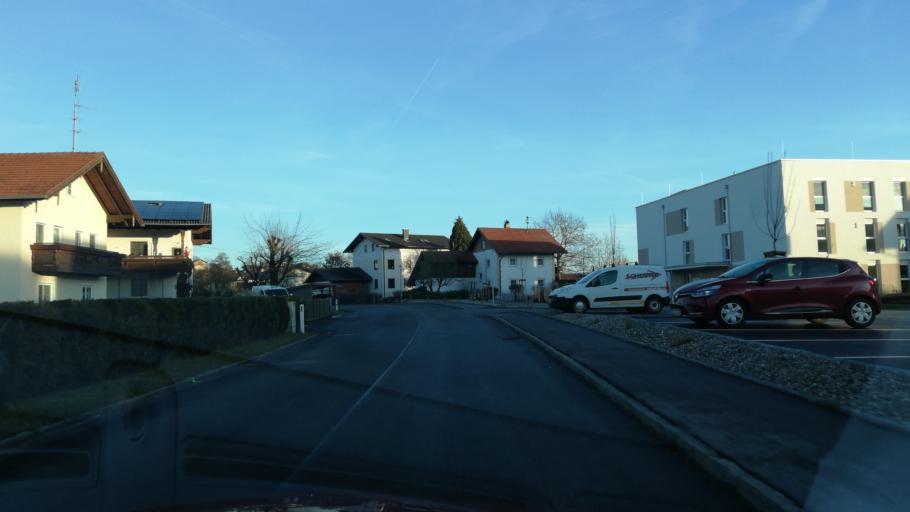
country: DE
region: Bavaria
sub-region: Upper Bavaria
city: Fridolfing
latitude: 48.0449
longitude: 12.8393
